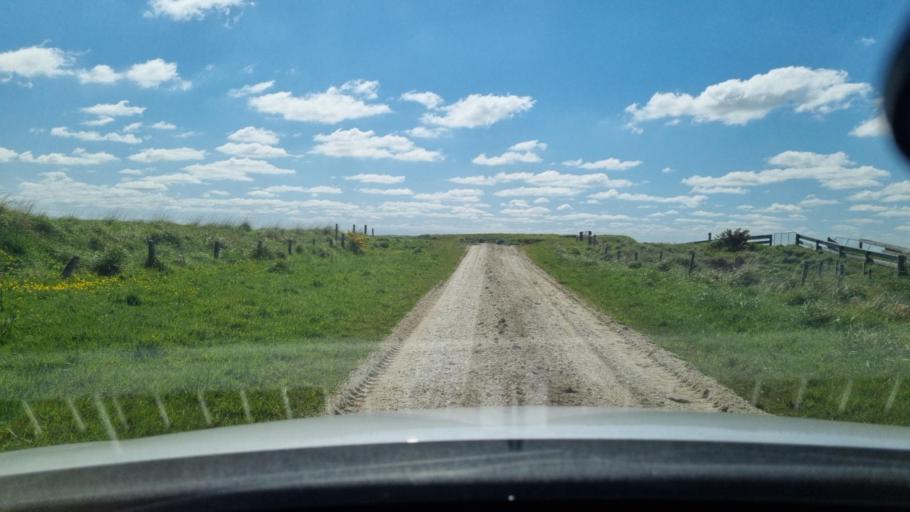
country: NZ
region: Southland
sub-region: Invercargill City
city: Invercargill
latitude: -46.3867
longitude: 168.2579
